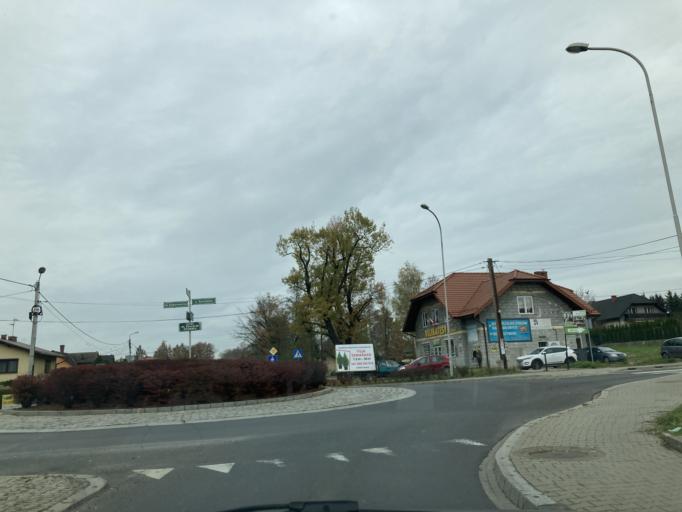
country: PL
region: Silesian Voivodeship
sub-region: Bielsko-Biala
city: Bielsko-Biala
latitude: 49.8571
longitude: 19.0486
